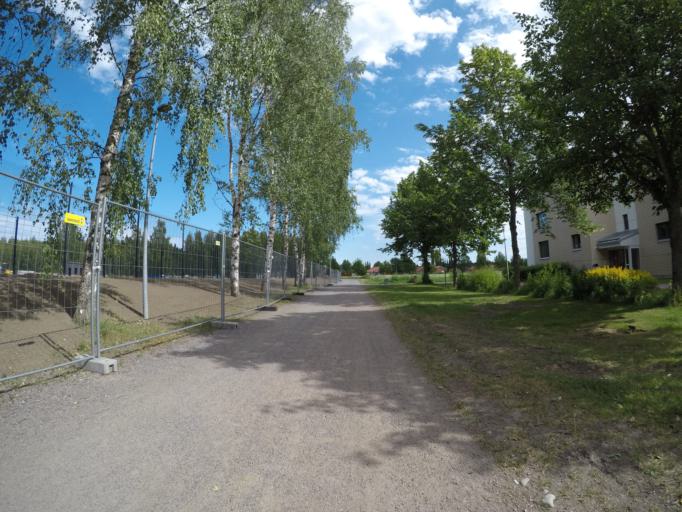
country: FI
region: Haeme
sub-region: Haemeenlinna
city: Haemeenlinna
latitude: 60.9811
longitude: 24.4260
